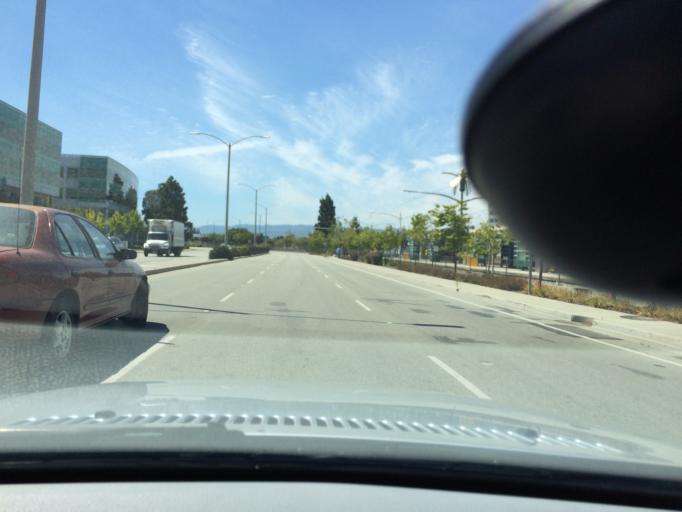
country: US
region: California
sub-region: Santa Clara County
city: Sunnyvale
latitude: 37.4103
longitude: -122.0266
